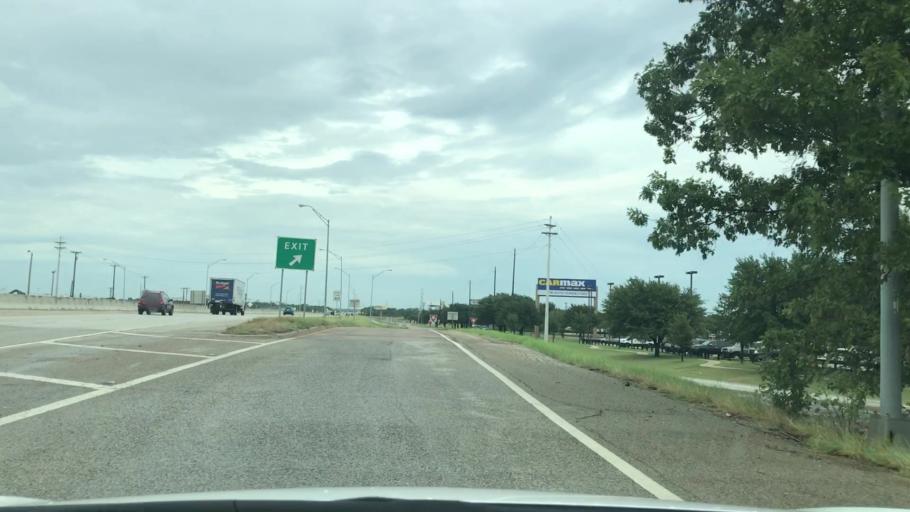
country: US
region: Texas
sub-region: Dallas County
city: Irving
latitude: 32.8401
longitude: -96.9035
